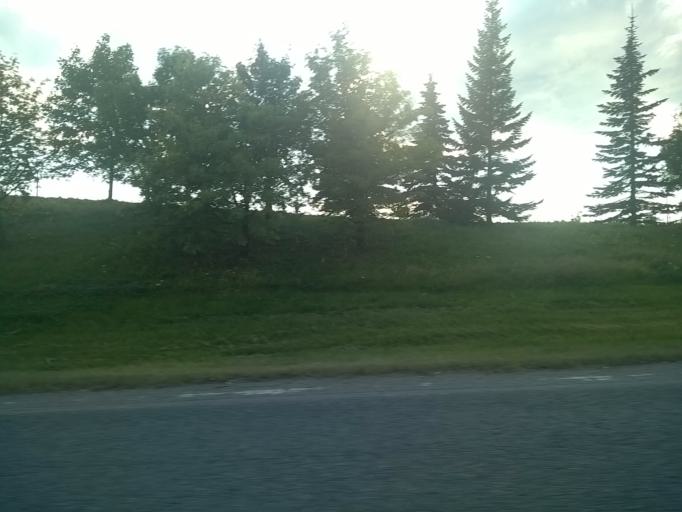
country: FI
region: Pirkanmaa
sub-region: Tampere
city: Tampere
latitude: 61.4775
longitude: 23.7750
